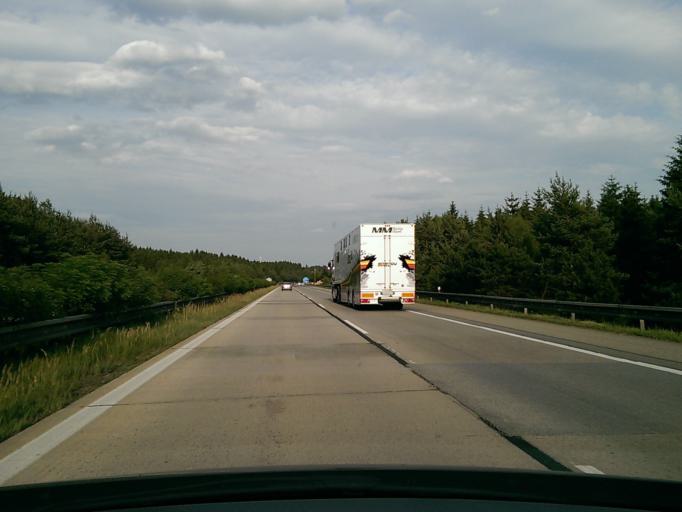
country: CZ
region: Vysocina
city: Velky Beranov
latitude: 49.4234
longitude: 15.6830
